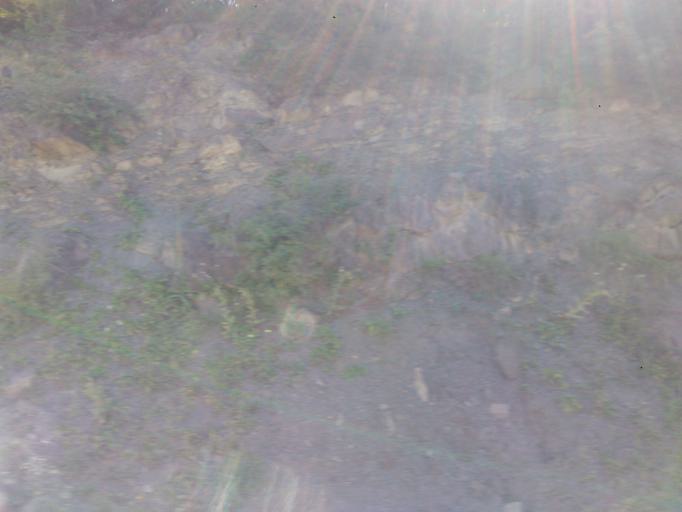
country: GE
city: Zhinvali
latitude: 42.1819
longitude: 44.8127
